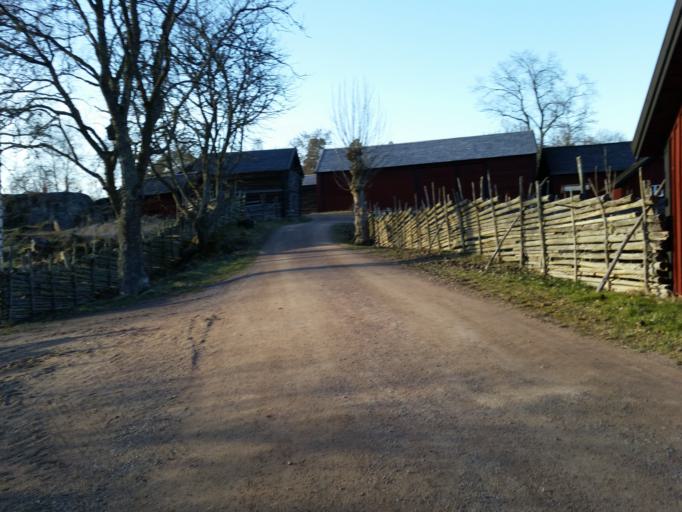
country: SE
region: Kalmar
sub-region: Oskarshamns Kommun
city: Oskarshamn
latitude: 57.3452
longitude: 16.4658
